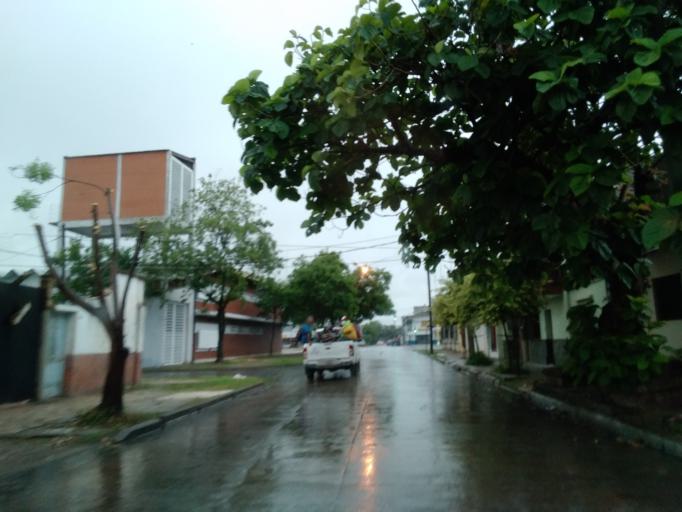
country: AR
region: Corrientes
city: Corrientes
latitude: -27.4782
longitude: -58.8237
